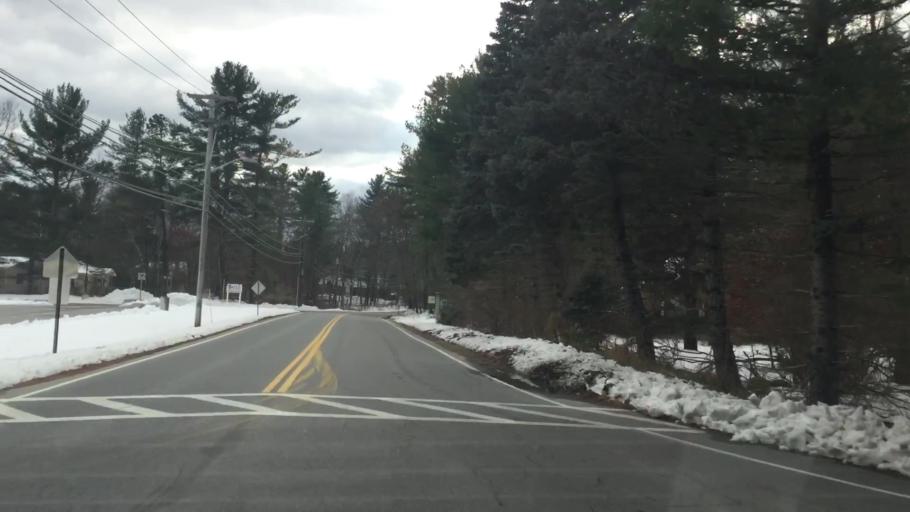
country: US
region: New Hampshire
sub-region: Hillsborough County
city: Pelham
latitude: 42.7230
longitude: -71.3330
